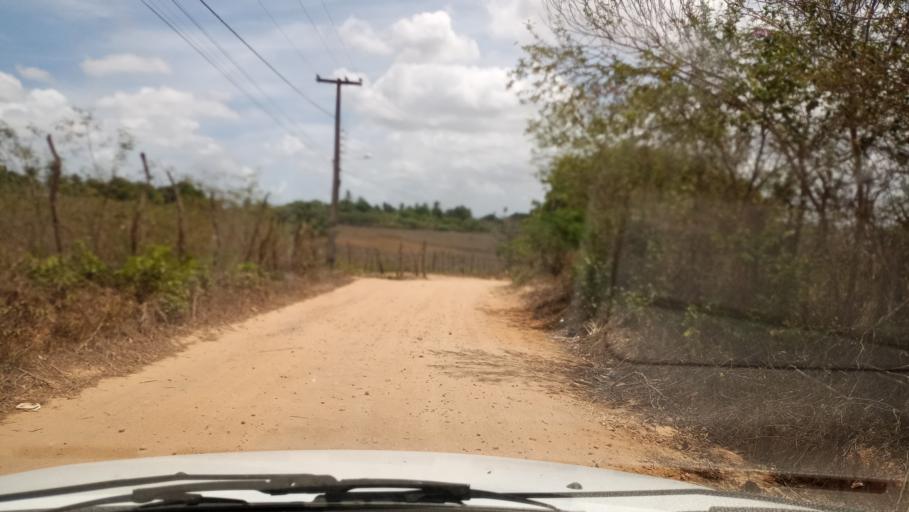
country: BR
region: Rio Grande do Norte
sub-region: Goianinha
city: Goianinha
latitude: -6.2880
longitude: -35.2856
